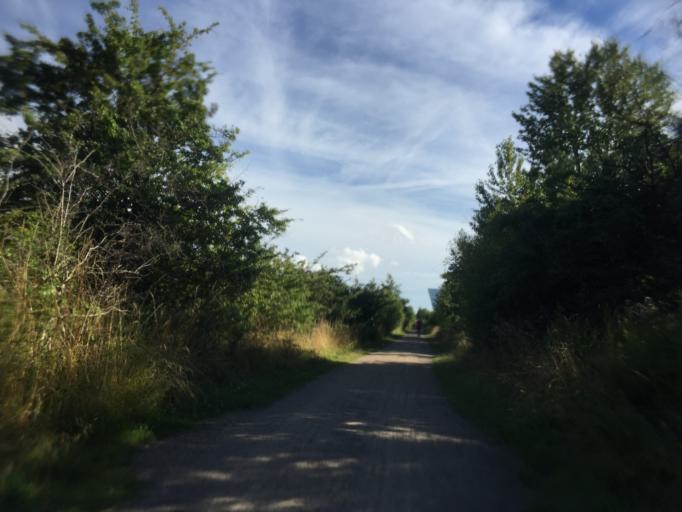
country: DK
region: Capital Region
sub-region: Tarnby Kommune
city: Tarnby
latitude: 55.6499
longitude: 12.5824
